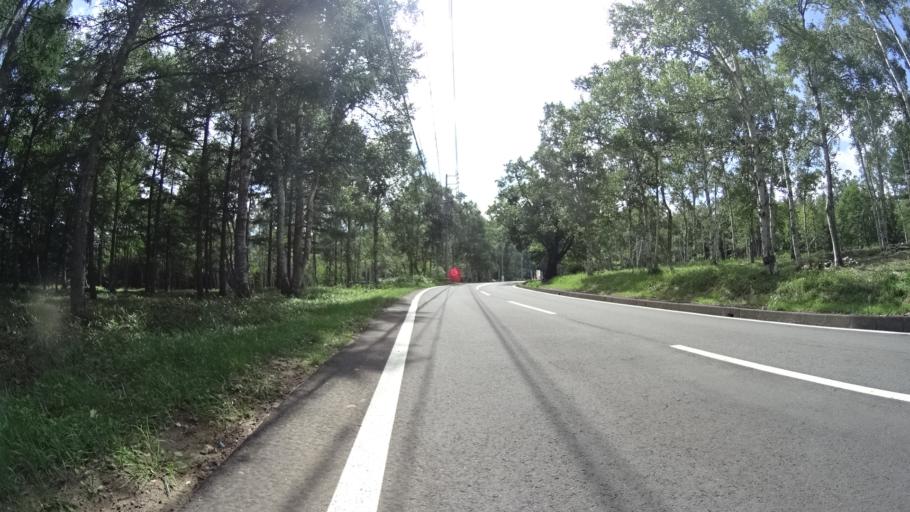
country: JP
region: Nagano
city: Saku
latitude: 36.0507
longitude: 138.4172
